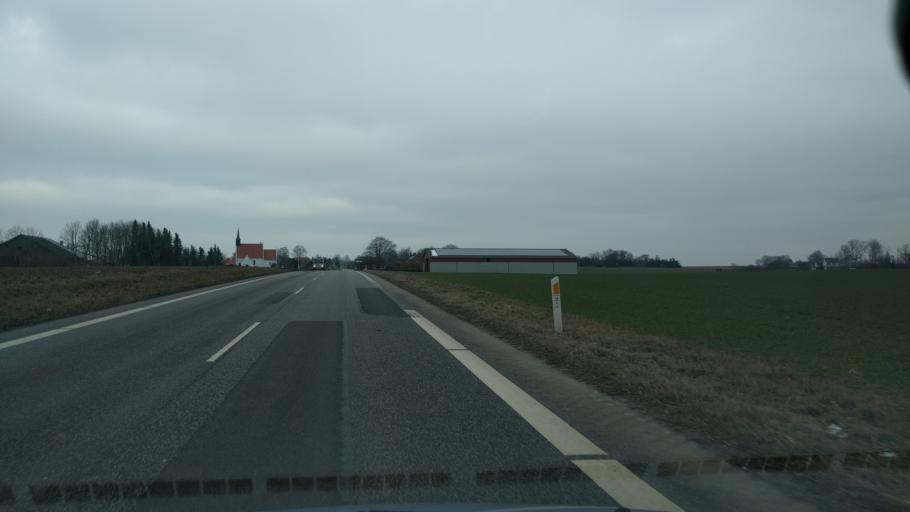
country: DK
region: Zealand
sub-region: Guldborgsund Kommune
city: Stubbekobing
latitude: 54.8578
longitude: 12.0170
